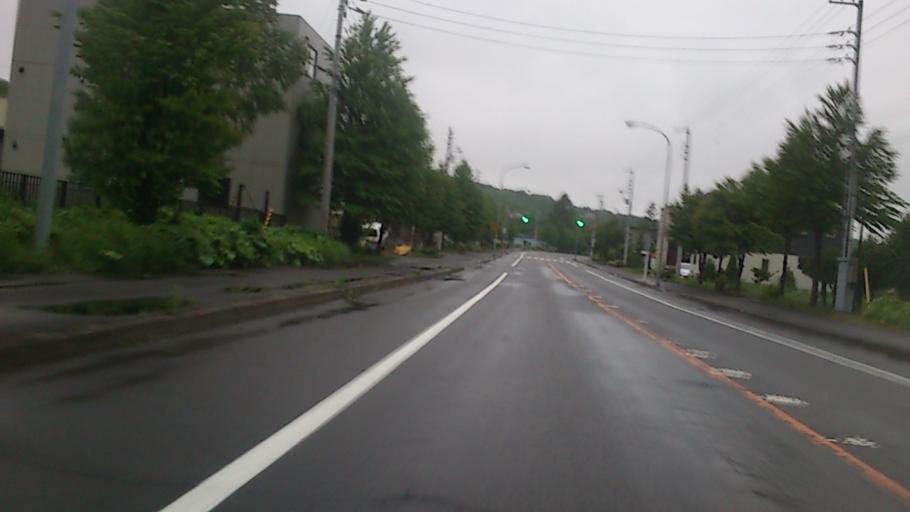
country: JP
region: Hokkaido
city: Chitose
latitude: 42.8166
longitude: 141.6076
